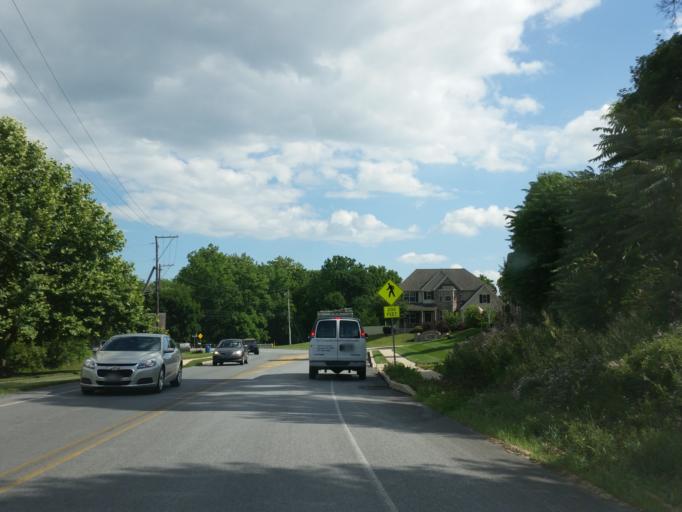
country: US
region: Pennsylvania
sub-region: Lancaster County
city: Lampeter
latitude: 40.0276
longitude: -76.2432
